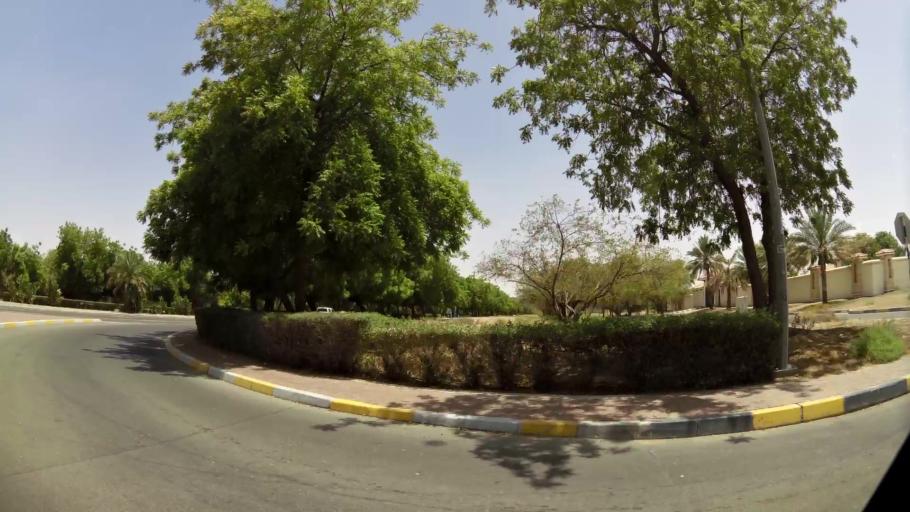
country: OM
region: Al Buraimi
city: Al Buraymi
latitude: 24.2567
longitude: 55.7197
